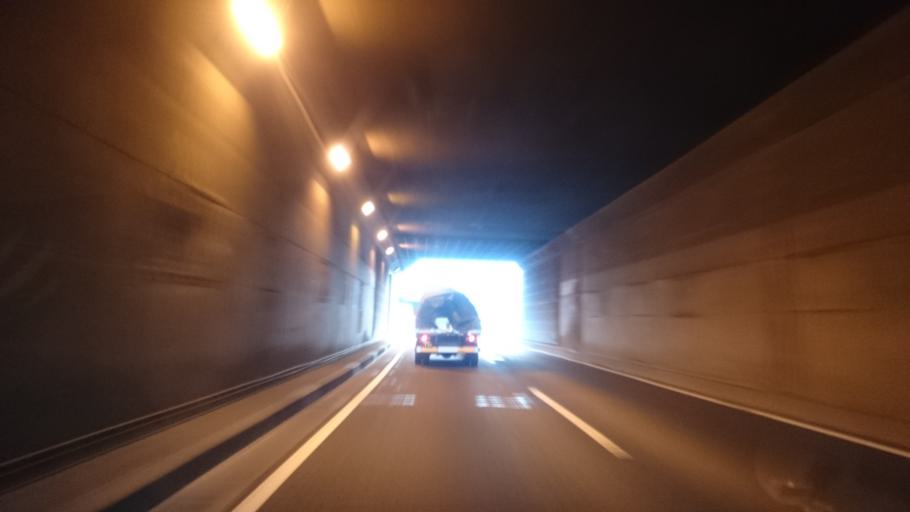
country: JP
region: Saitama
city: Ageoshimo
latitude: 35.9618
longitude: 139.6289
